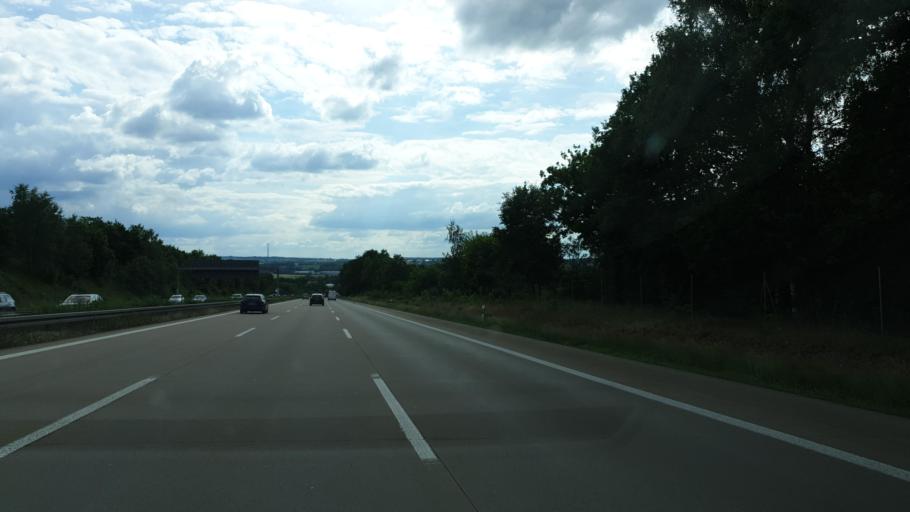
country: DE
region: Saxony
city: Frankenberg
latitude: 50.9246
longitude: 13.0432
